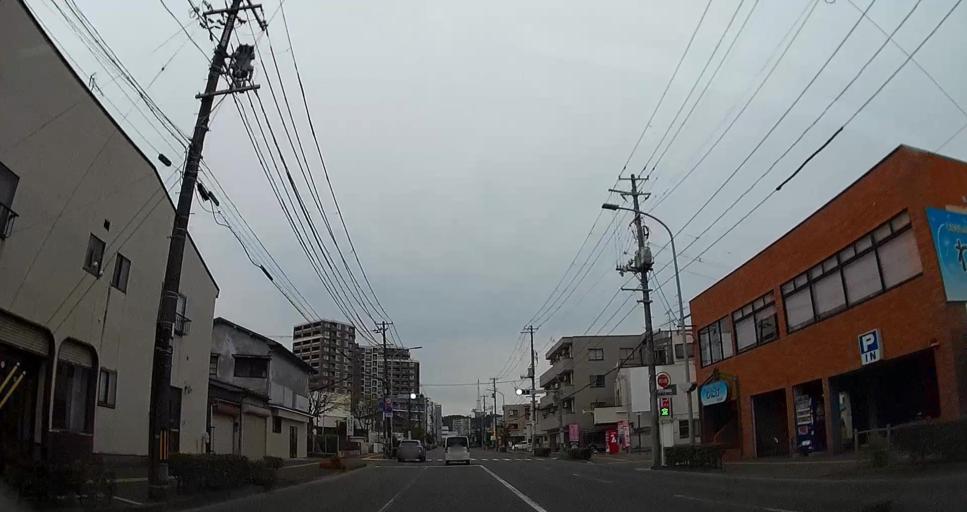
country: JP
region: Miyagi
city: Sendai
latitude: 38.2289
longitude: 140.8939
